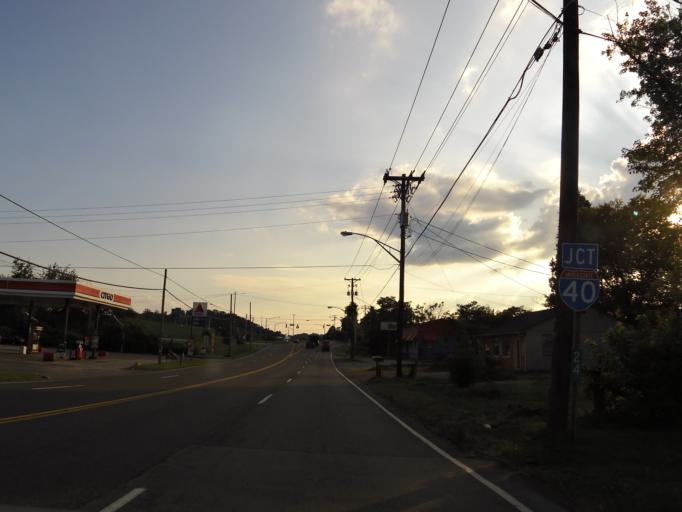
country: US
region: Tennessee
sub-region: Knox County
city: Knoxville
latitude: 36.0102
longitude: -83.8712
